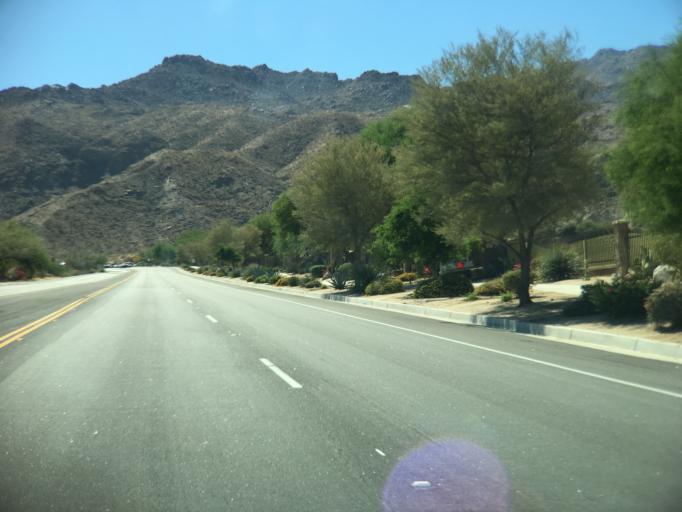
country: US
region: California
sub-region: Riverside County
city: Palm Desert
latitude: 33.6760
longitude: -116.4079
